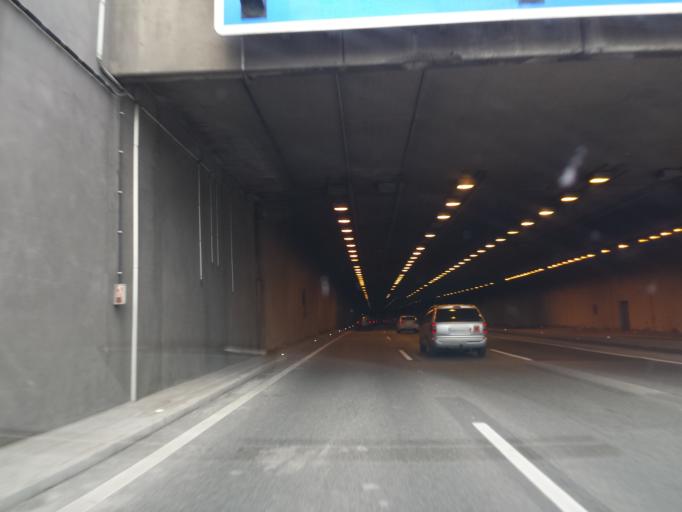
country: AT
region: Vienna
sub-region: Wien Stadt
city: Vienna
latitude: 48.2208
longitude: 16.4265
